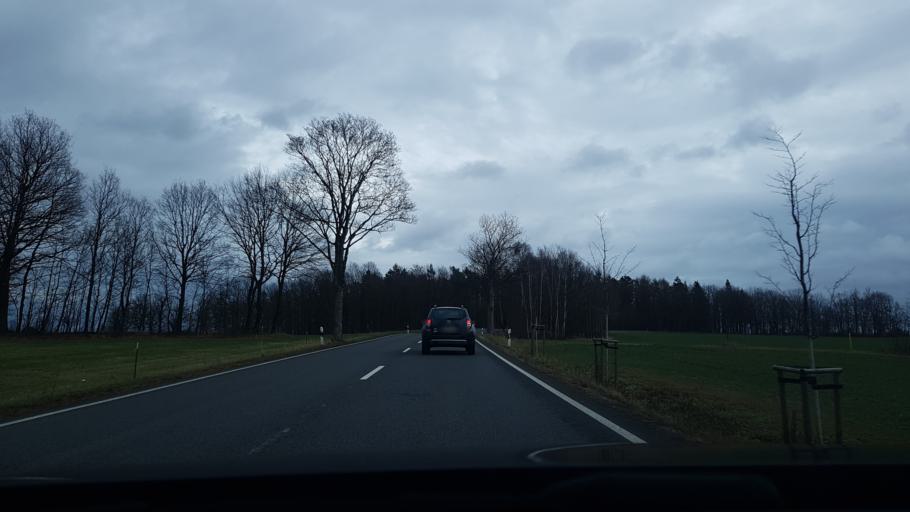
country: DE
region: Saxony
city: Dohma
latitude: 50.8922
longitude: 13.9493
